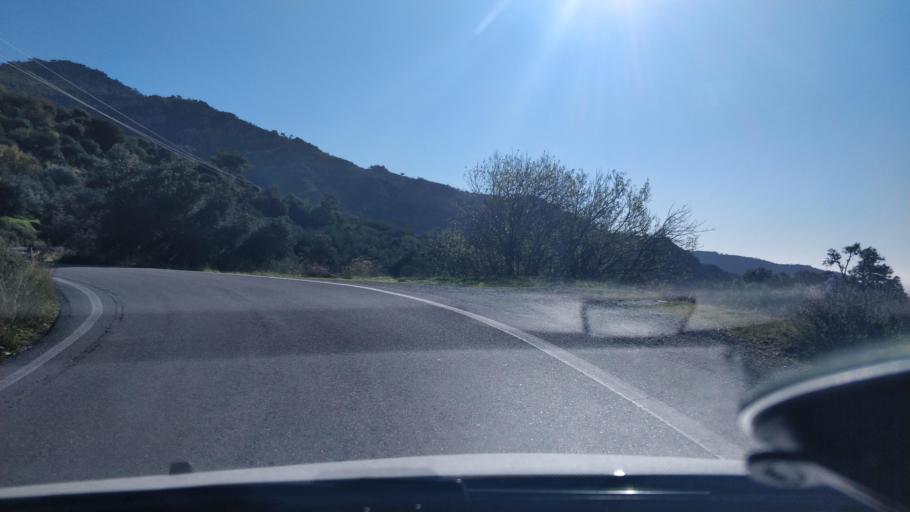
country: GR
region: Crete
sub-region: Nomos Lasithiou
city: Kritsa
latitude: 35.0795
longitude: 25.5957
